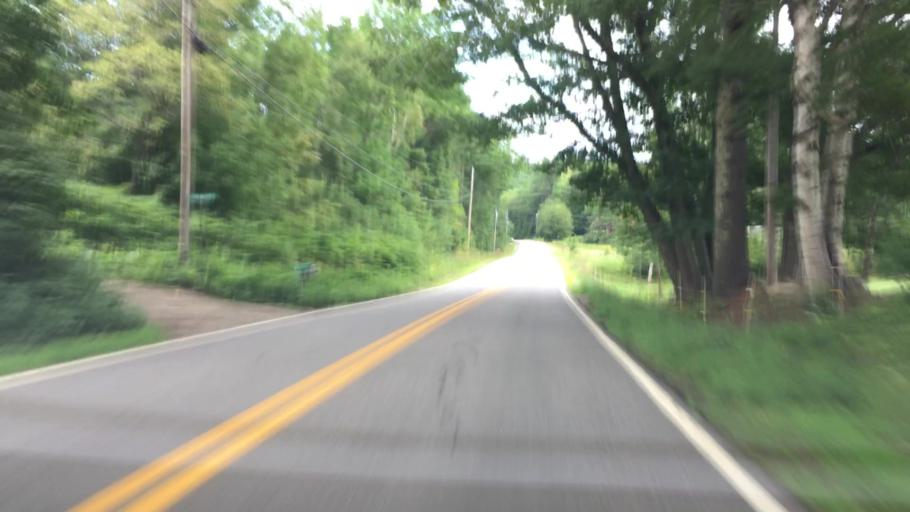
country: US
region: Maine
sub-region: Waldo County
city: Lincolnville
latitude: 44.3261
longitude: -69.0646
